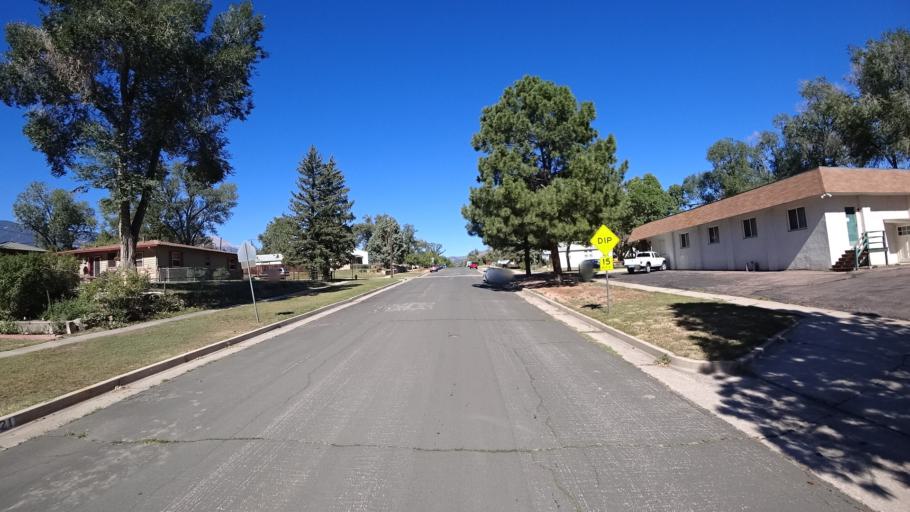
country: US
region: Colorado
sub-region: El Paso County
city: Colorado Springs
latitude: 38.8444
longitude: -104.8488
